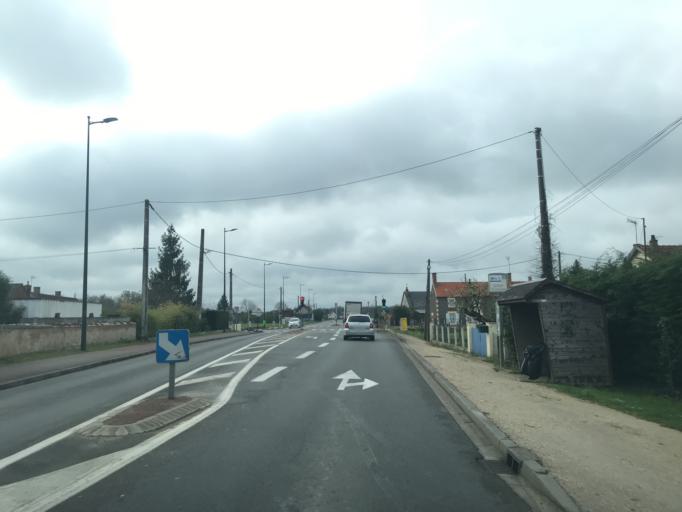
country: FR
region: Centre
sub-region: Departement du Loiret
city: Bray-en-Val
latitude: 47.8311
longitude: 2.3682
